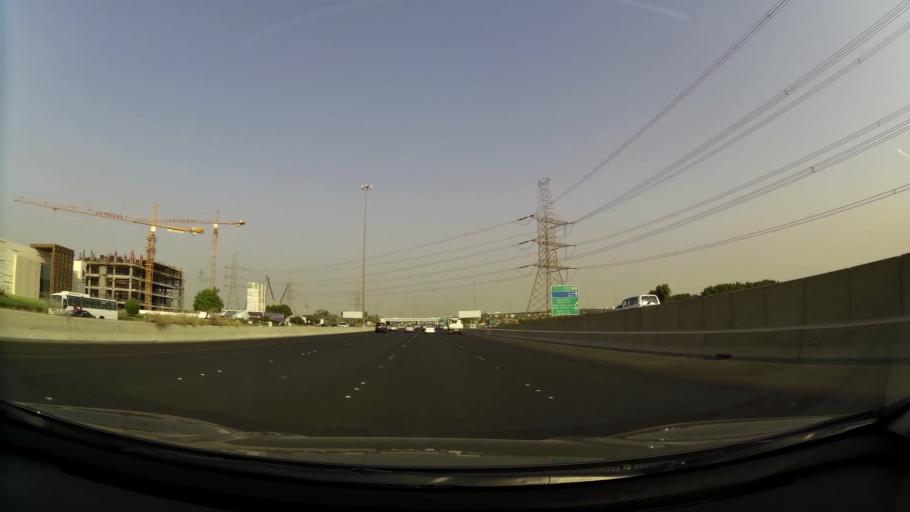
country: KW
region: Al Asimah
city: Ar Rabiyah
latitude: 29.3012
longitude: 47.9406
